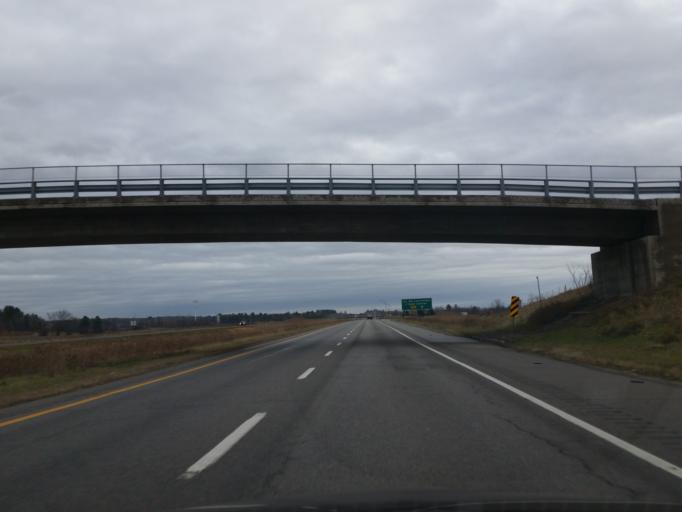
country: CA
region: Quebec
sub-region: Outaouais
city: Val-des-Monts
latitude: 45.5291
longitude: -75.5096
